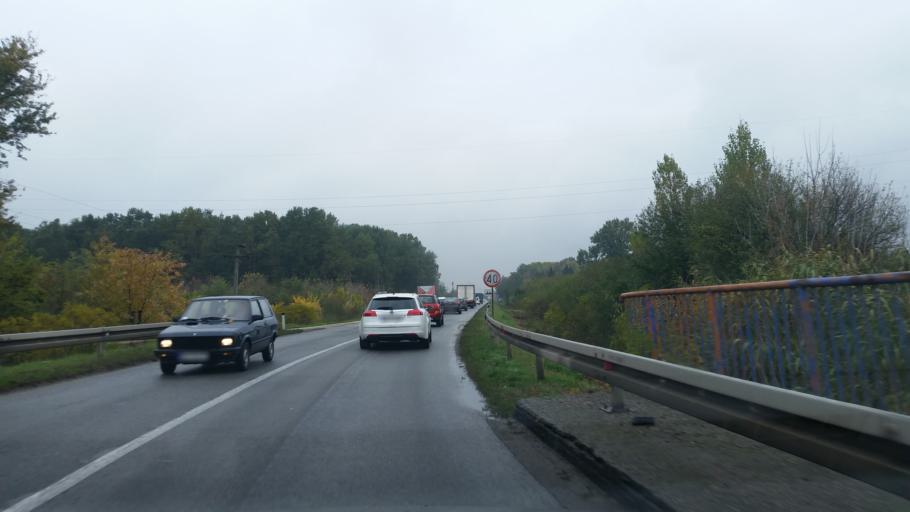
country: RS
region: Central Serbia
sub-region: Belgrade
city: Zemun
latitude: 44.9246
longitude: 20.4362
